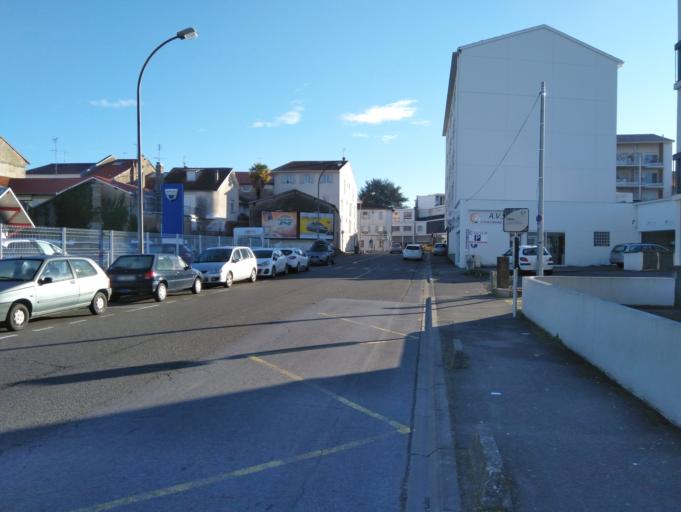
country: FR
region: Aquitaine
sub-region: Departement des Landes
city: Dax
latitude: 43.7149
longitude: -1.0555
